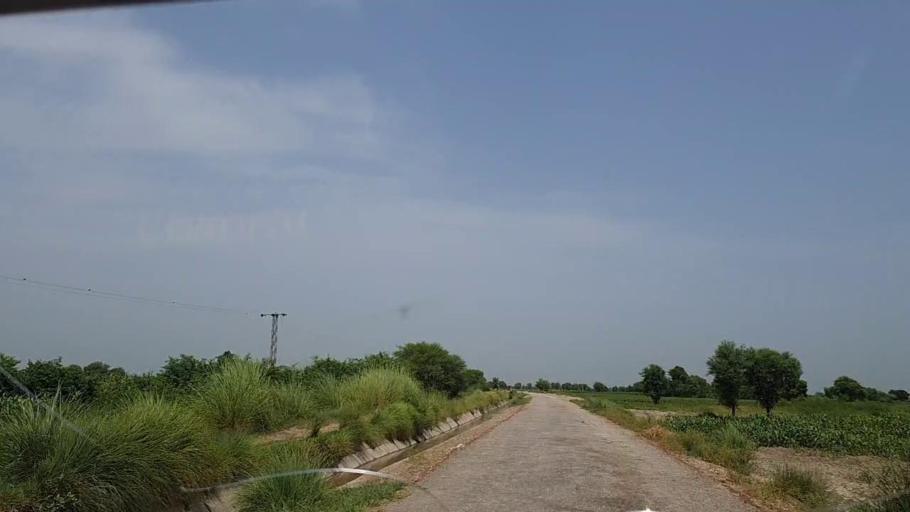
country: PK
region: Sindh
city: Tharu Shah
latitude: 26.9283
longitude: 68.0684
